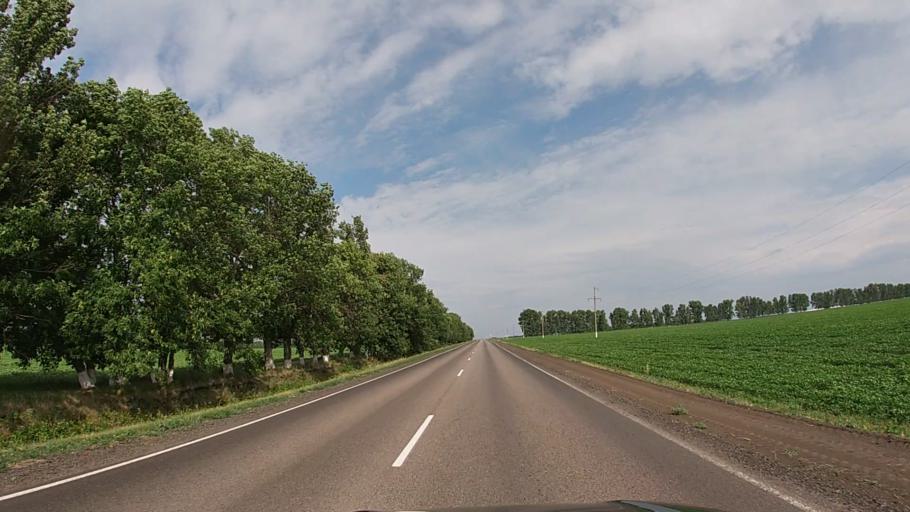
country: RU
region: Belgorod
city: Krasnaya Yaruga
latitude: 50.8041
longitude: 35.5510
